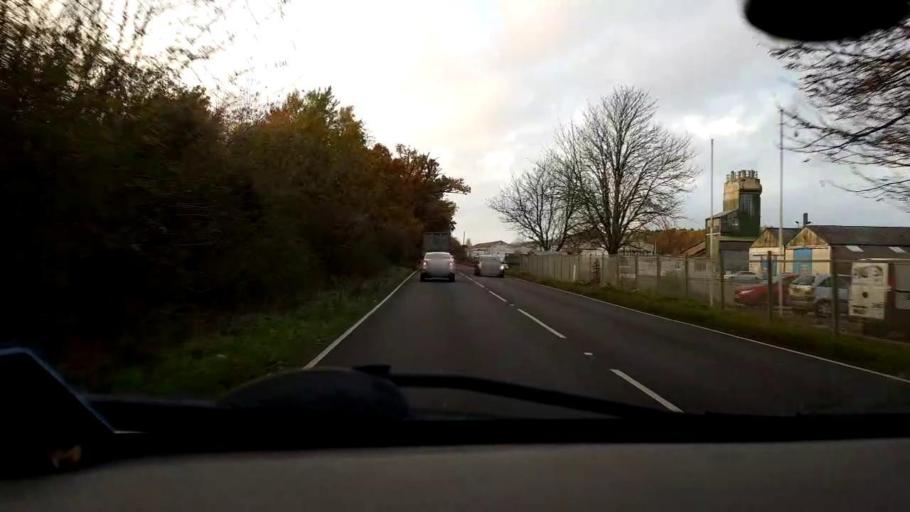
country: GB
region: England
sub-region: Norfolk
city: Costessey
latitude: 52.7153
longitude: 1.1310
